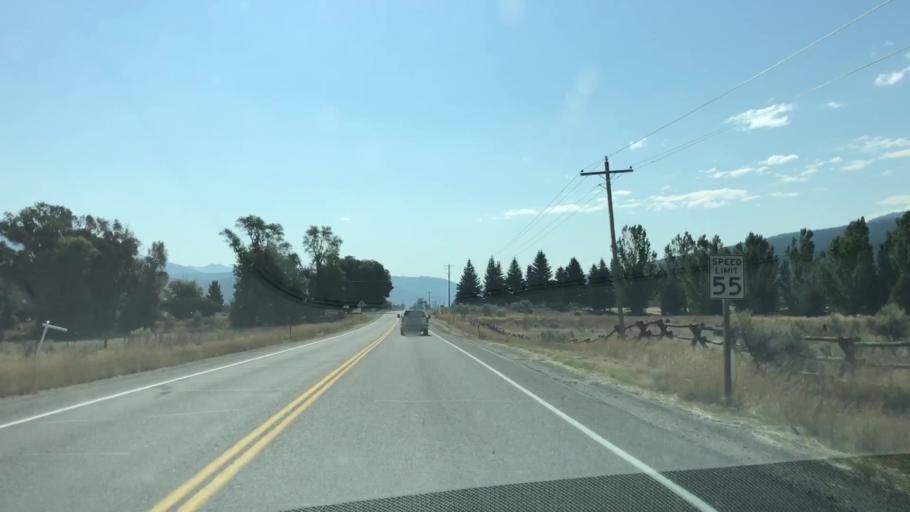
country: US
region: Idaho
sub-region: Teton County
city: Victor
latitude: 43.4017
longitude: -111.2885
